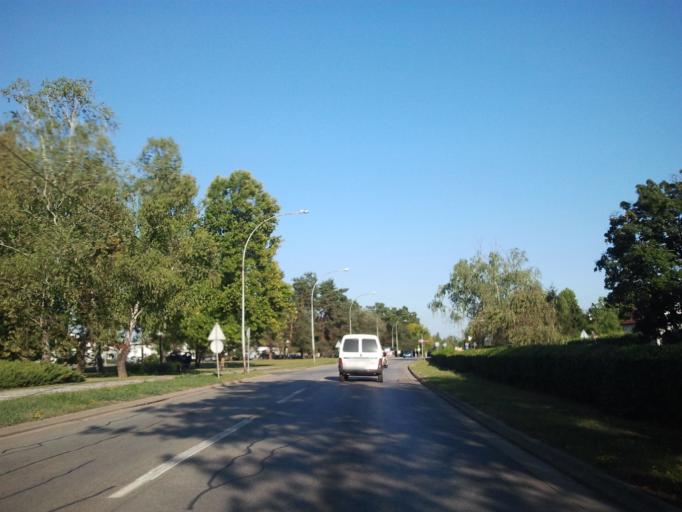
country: HR
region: Sisacko-Moslavacka
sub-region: Grad Sisak
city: Sisak
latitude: 45.4711
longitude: 16.3712
